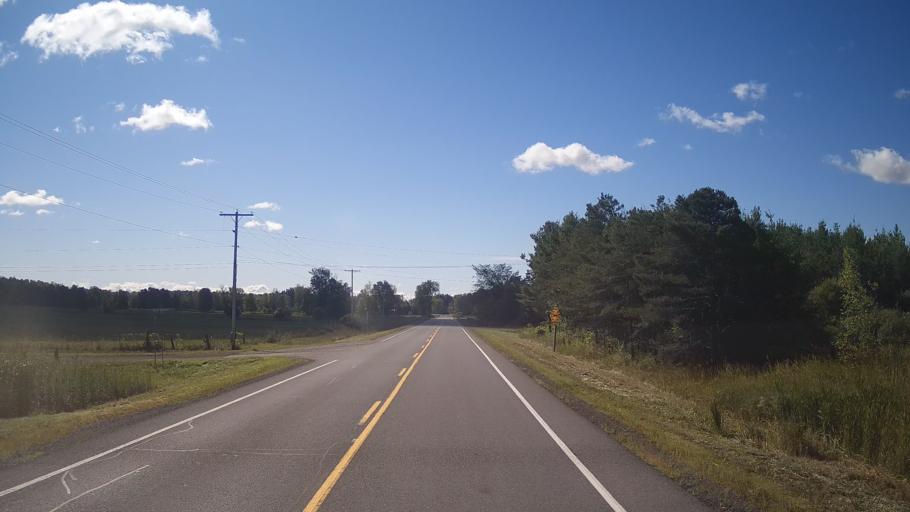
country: CA
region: Ontario
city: Prescott
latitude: 44.9081
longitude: -75.4042
